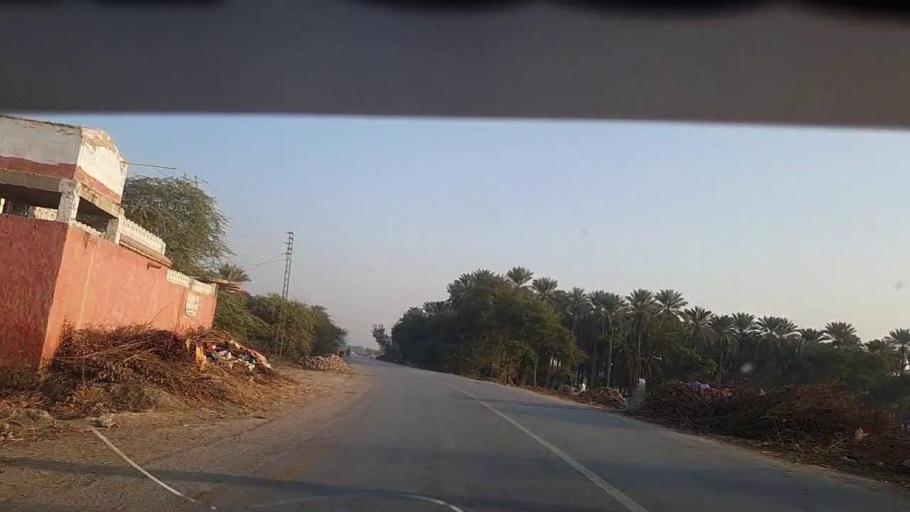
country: PK
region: Sindh
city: Ranipur
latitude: 27.2609
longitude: 68.5257
